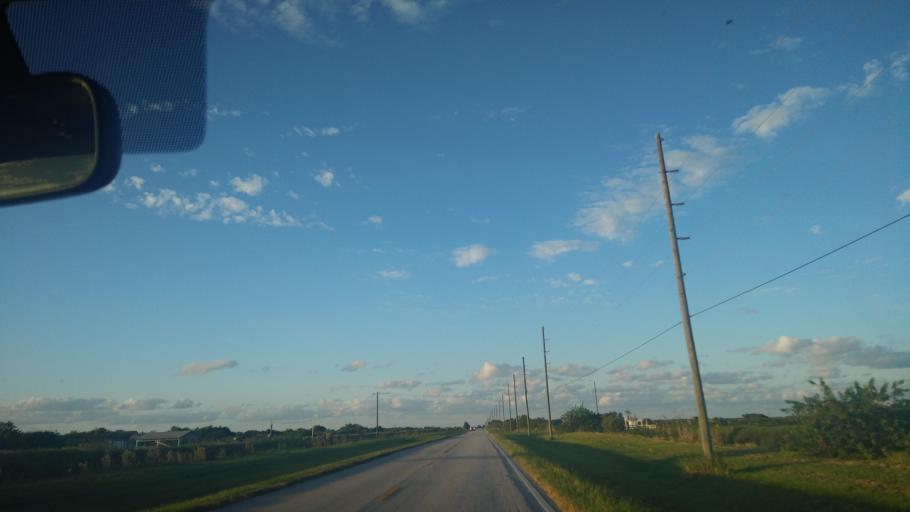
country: US
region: Florida
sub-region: Indian River County
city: Fellsmere
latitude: 27.7202
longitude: -80.6426
